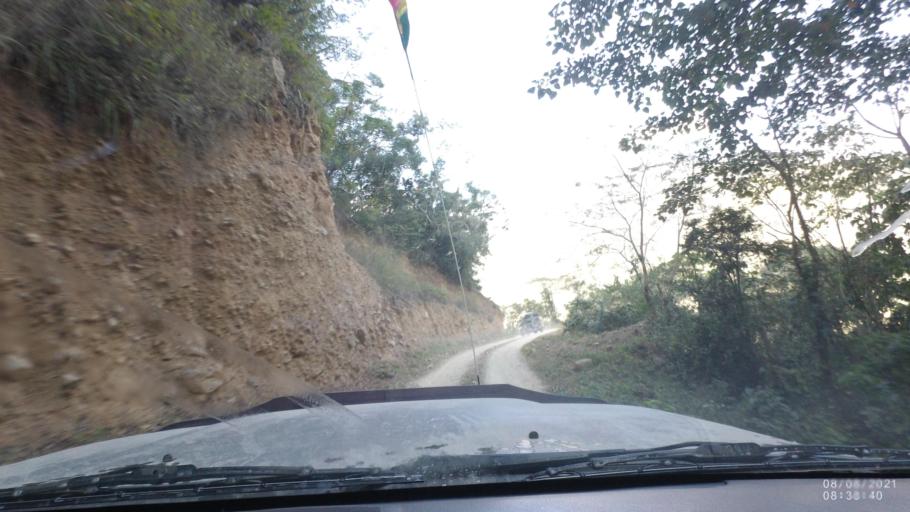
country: BO
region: La Paz
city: Quime
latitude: -16.5259
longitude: -66.7663
